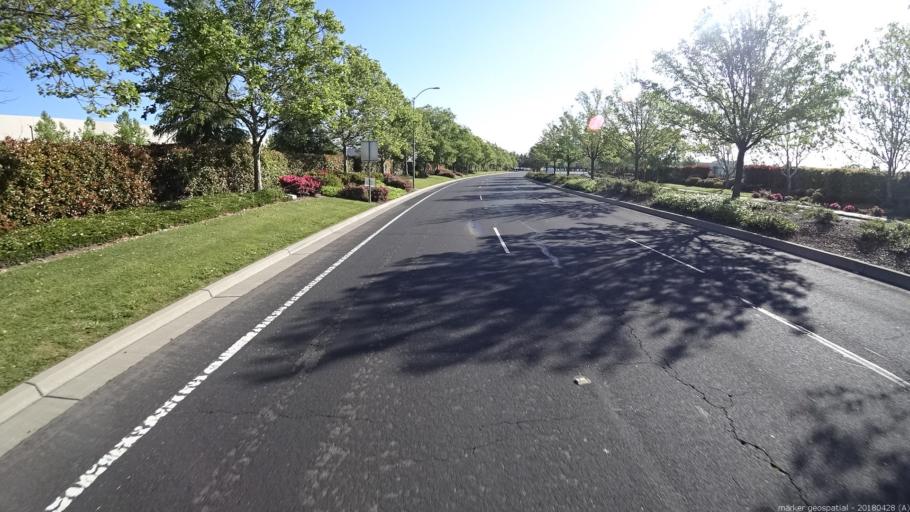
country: US
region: California
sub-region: Yolo County
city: West Sacramento
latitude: 38.5544
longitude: -121.5654
